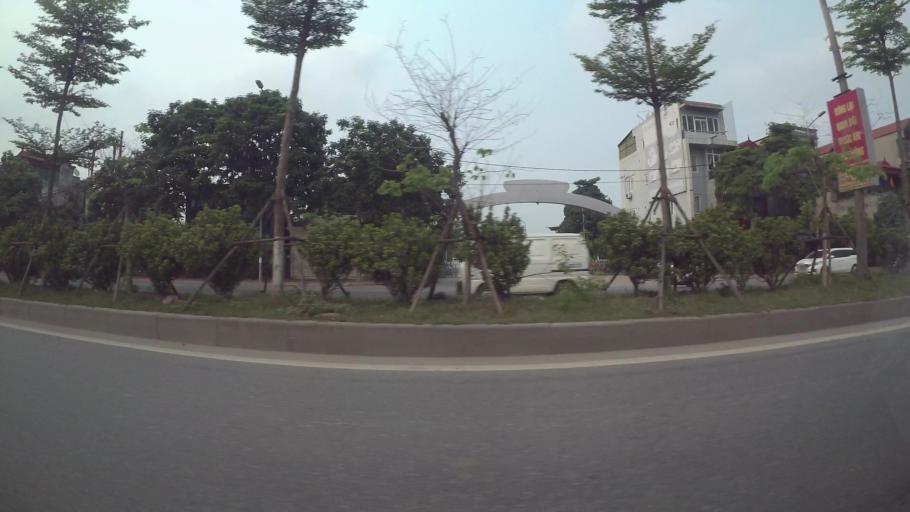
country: VN
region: Ha Noi
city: Trau Quy
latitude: 21.0267
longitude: 105.9242
